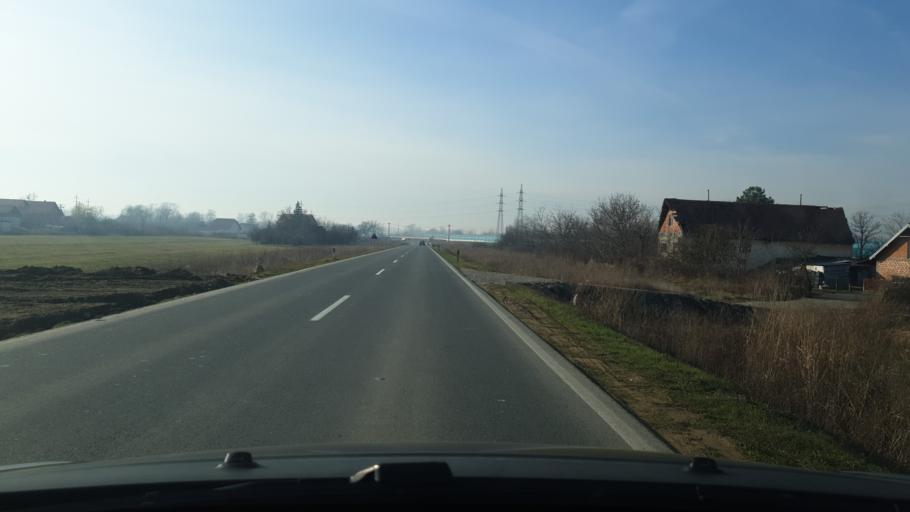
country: RS
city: Baric
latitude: 44.6485
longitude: 20.2299
